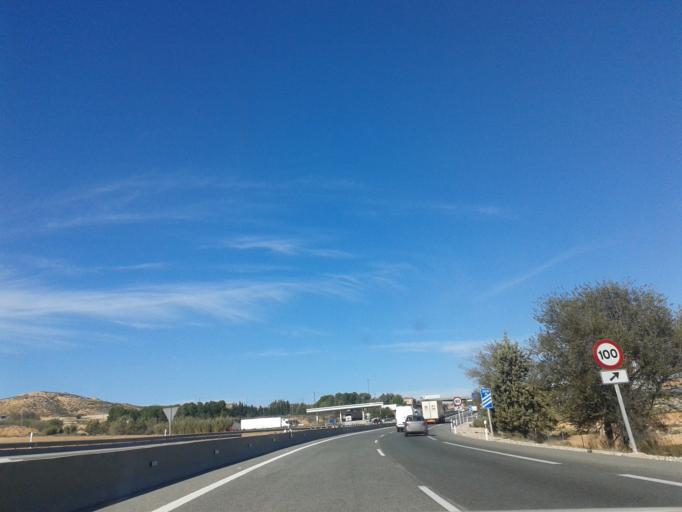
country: ES
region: Castille-La Mancha
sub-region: Provincia de Albacete
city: Caudete
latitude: 38.7264
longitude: -0.9381
